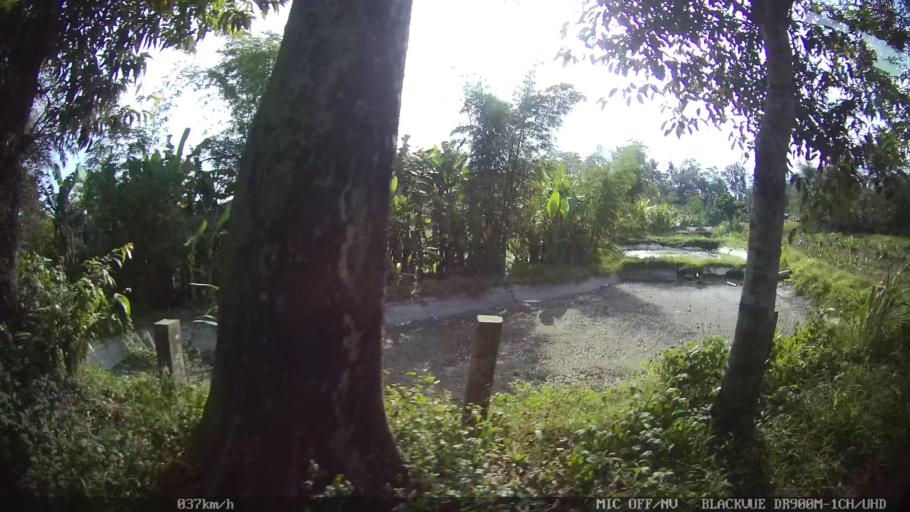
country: ID
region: Daerah Istimewa Yogyakarta
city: Depok
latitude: -7.7264
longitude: 110.4351
